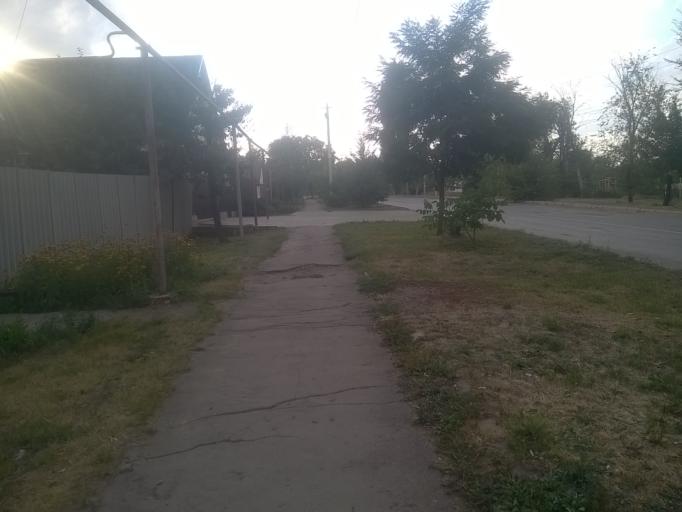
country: RU
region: Rostov
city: Donetsk
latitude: 48.3357
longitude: 39.9572
